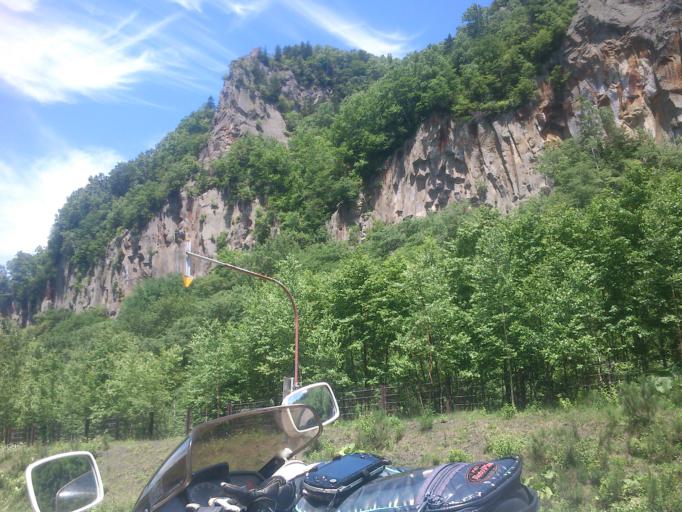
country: JP
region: Hokkaido
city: Kamikawa
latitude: 43.7636
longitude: 142.9167
